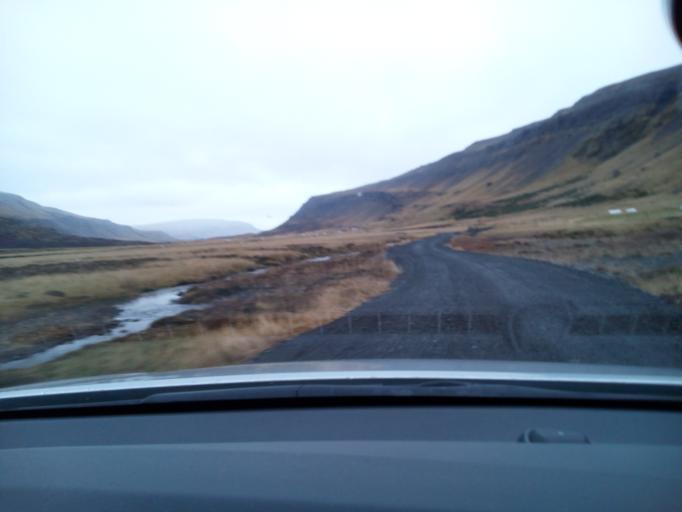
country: IS
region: South
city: Hveragerdi
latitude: 64.3630
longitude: -21.3091
